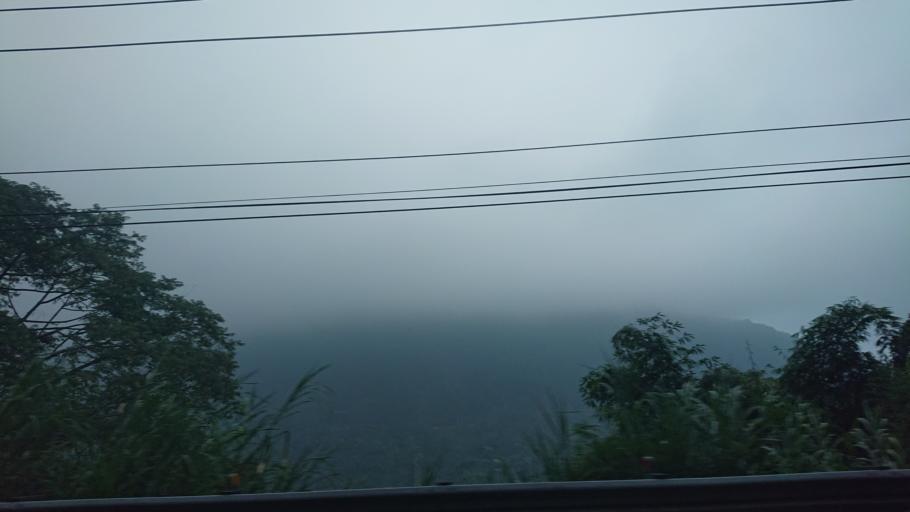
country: TW
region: Taiwan
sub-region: Chiayi
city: Jiayi Shi
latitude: 23.4712
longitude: 120.7100
